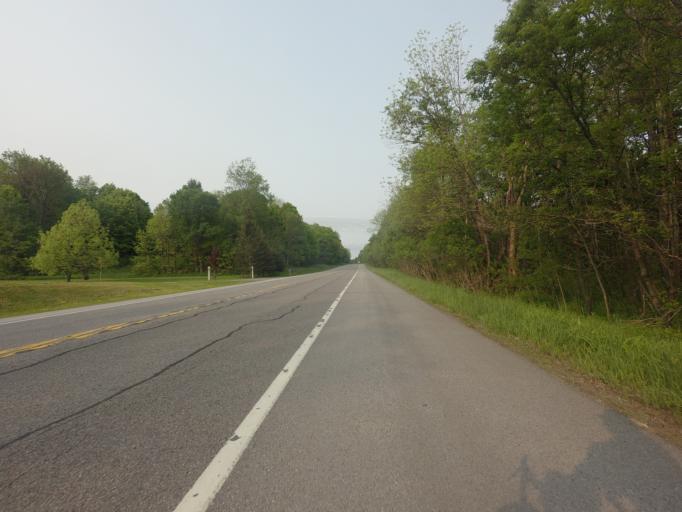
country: US
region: New York
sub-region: Jefferson County
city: Carthage
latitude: 44.0559
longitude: -75.5477
